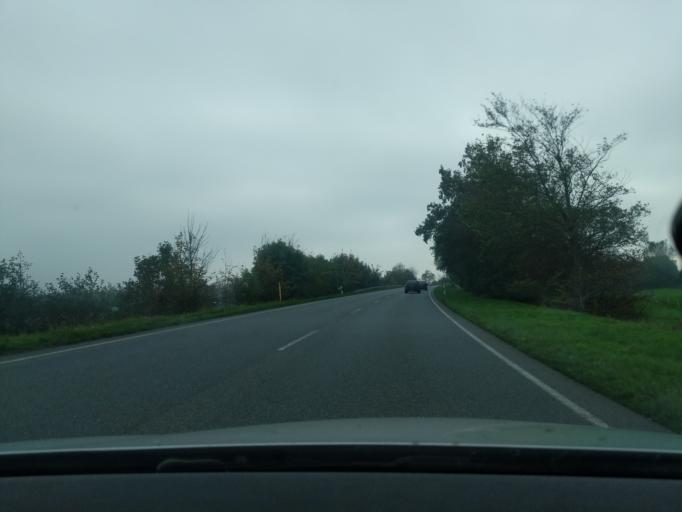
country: DE
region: Lower Saxony
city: Wanna
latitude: 53.8217
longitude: 8.7653
